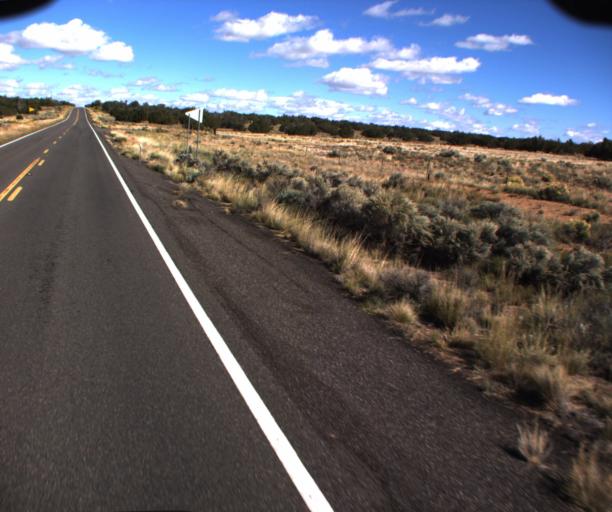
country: US
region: Arizona
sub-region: Apache County
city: Saint Johns
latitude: 34.8249
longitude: -109.2374
